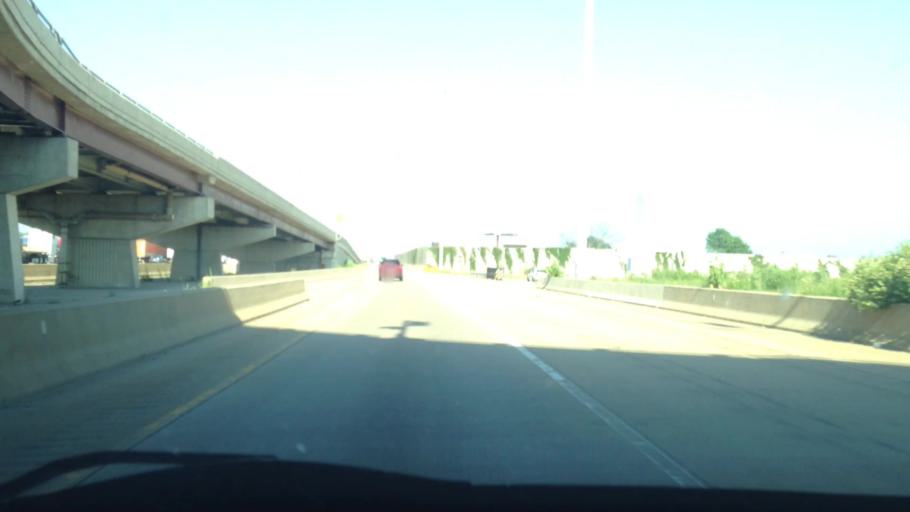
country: US
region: Illinois
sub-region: Cook County
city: Lansing
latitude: 41.5773
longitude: -87.5586
